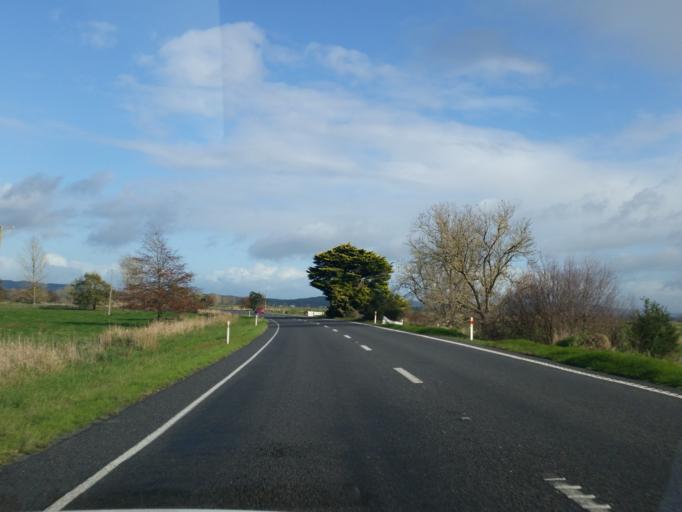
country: NZ
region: Waikato
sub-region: Hauraki District
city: Ngatea
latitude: -37.2761
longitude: 175.4658
